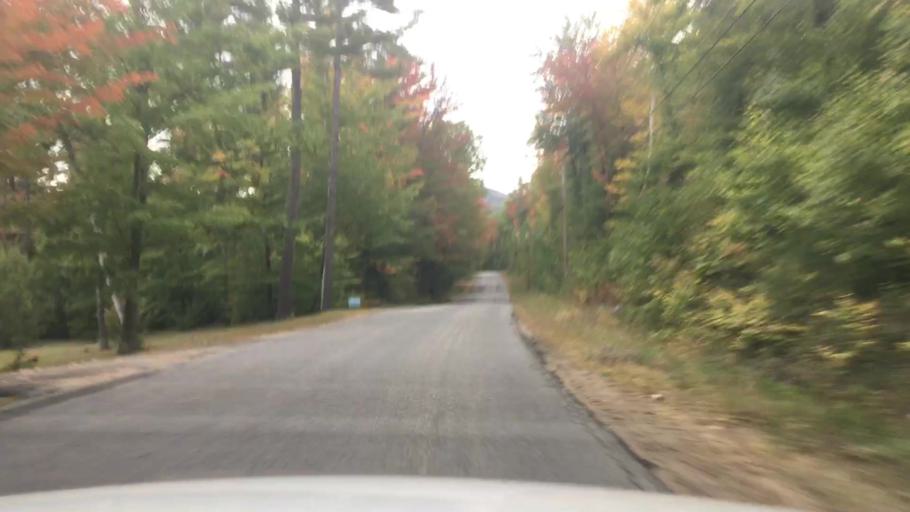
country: US
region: Maine
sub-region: Oxford County
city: Bethel
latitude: 44.4744
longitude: -70.7838
